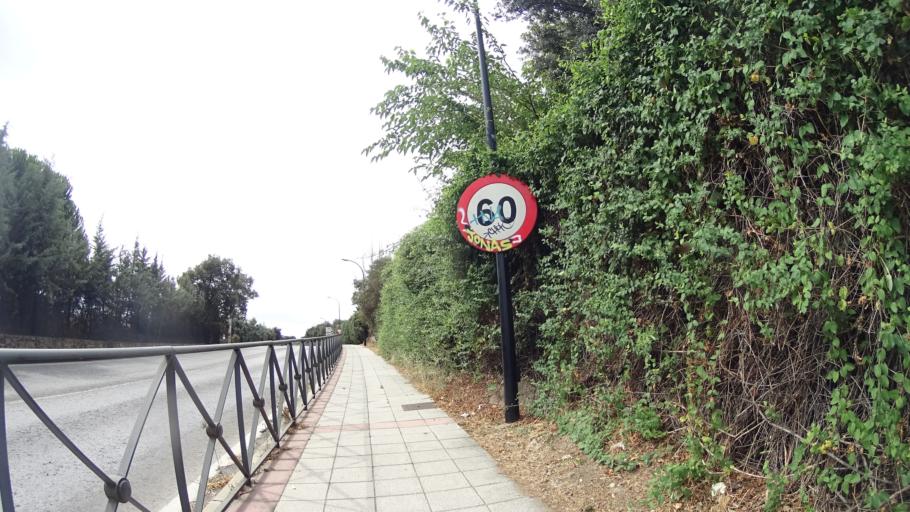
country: ES
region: Madrid
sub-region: Provincia de Madrid
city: Galapagar
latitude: 40.5875
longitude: -4.0119
